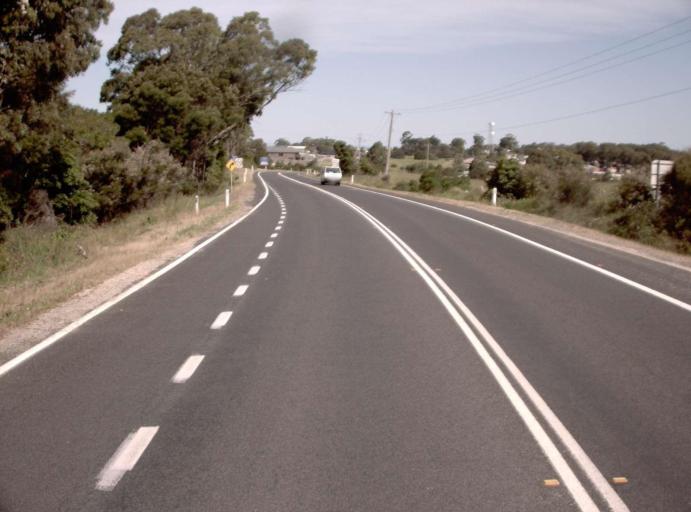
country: AU
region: Victoria
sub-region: East Gippsland
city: Lakes Entrance
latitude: -37.8720
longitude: 147.9594
